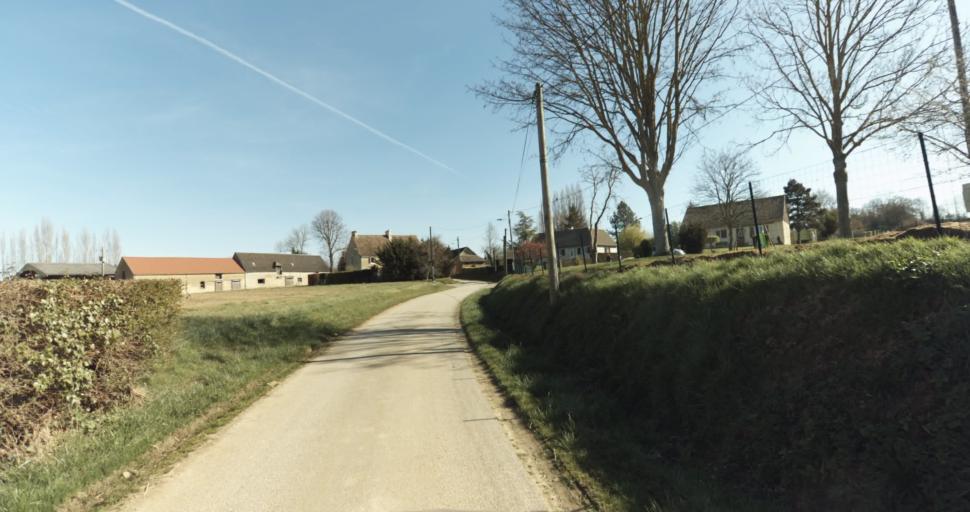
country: FR
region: Lower Normandy
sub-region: Departement du Calvados
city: Saint-Pierre-sur-Dives
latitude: 49.0373
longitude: -0.0066
